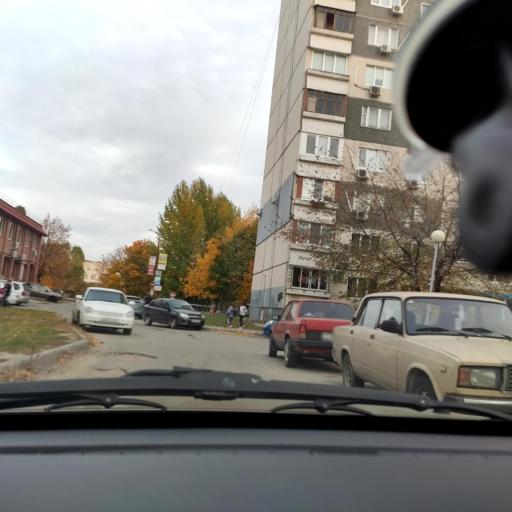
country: RU
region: Samara
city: Tol'yatti
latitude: 53.5374
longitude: 49.3462
